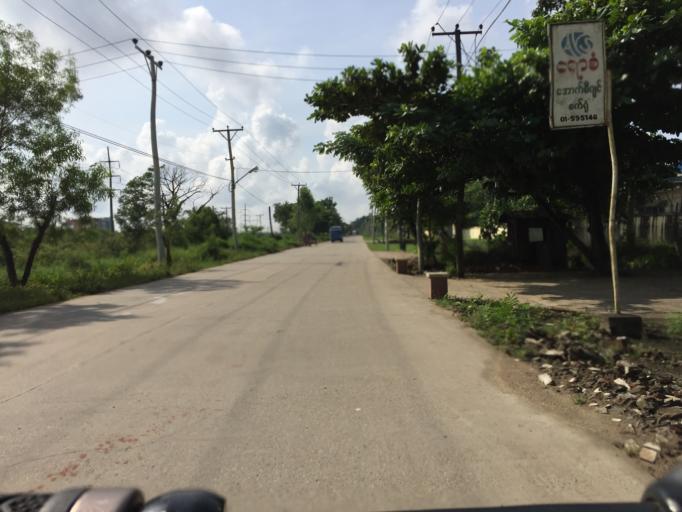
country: MM
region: Yangon
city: Syriam
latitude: 16.8310
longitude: 96.2222
